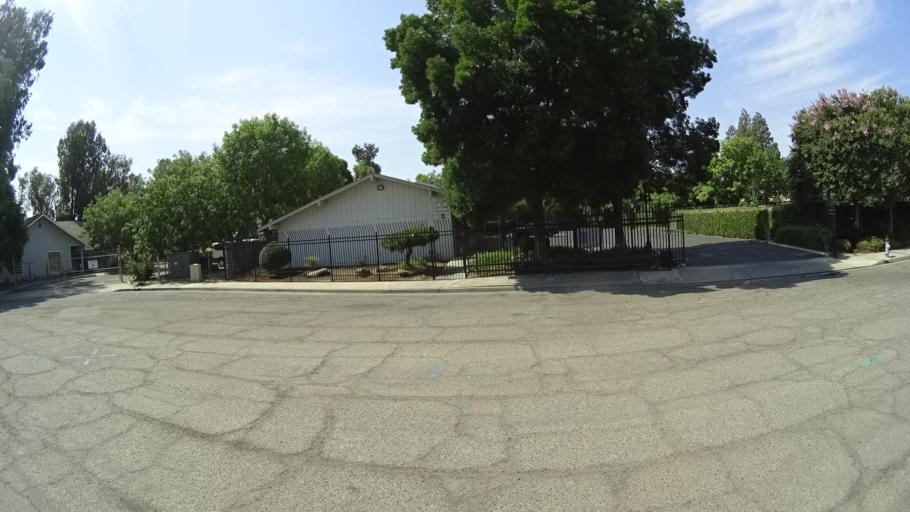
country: US
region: California
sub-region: Fresno County
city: Fresno
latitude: 36.7587
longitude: -119.8253
